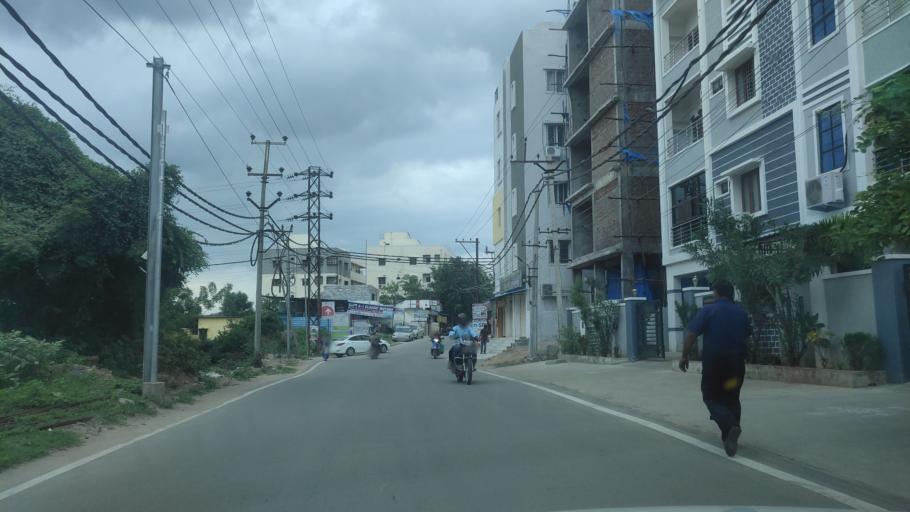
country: IN
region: Telangana
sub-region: Medak
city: Serilingampalle
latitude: 17.4999
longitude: 78.3492
